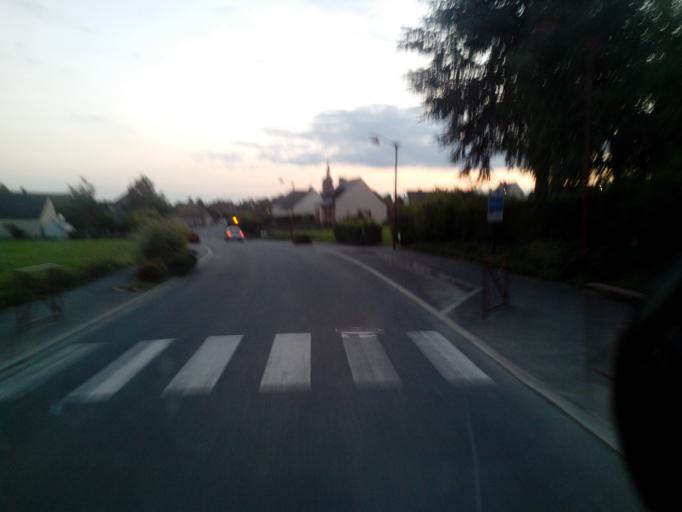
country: FR
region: Brittany
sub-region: Departement d'Ille-et-Vilaine
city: Iffendic
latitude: 48.1306
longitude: -2.0281
